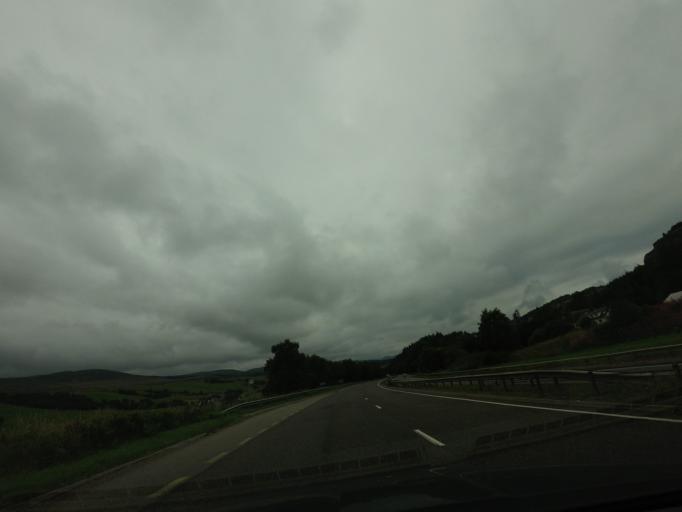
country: GB
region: Scotland
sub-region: Highland
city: Inverness
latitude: 57.4263
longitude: -4.1266
